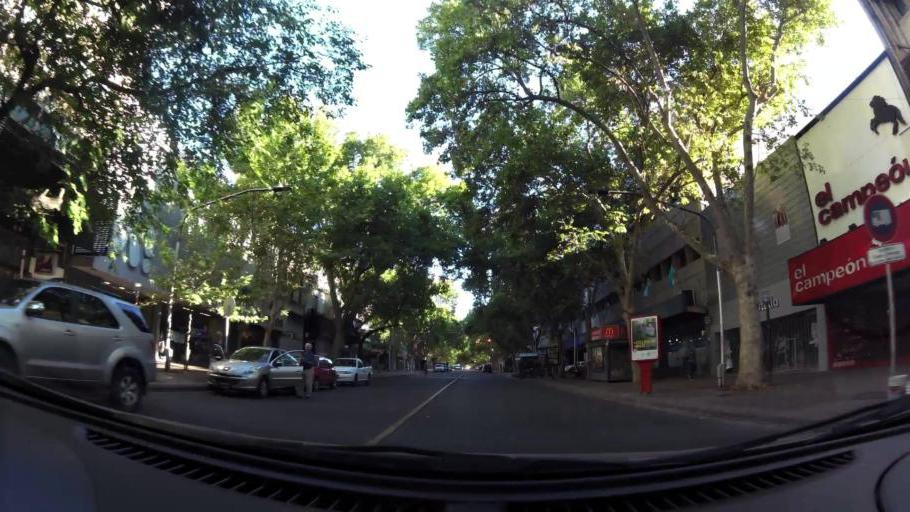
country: AR
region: Mendoza
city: Mendoza
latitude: -32.8879
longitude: -68.8388
